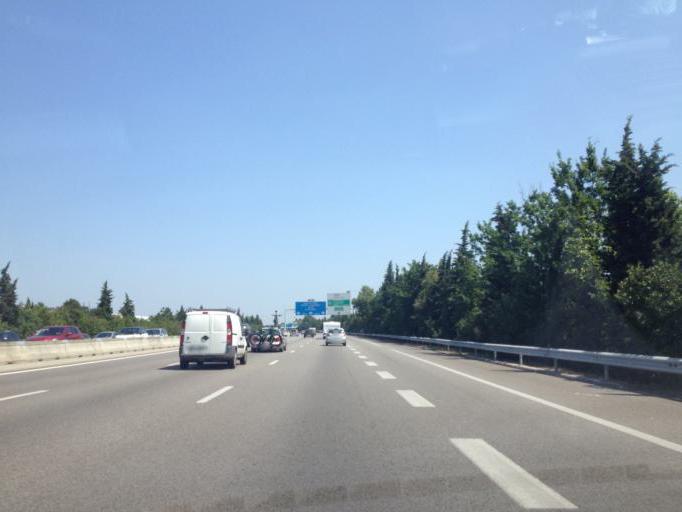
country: FR
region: Rhone-Alpes
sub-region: Departement de la Drome
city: Portes-les-Valence
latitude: 44.8947
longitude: 4.8732
